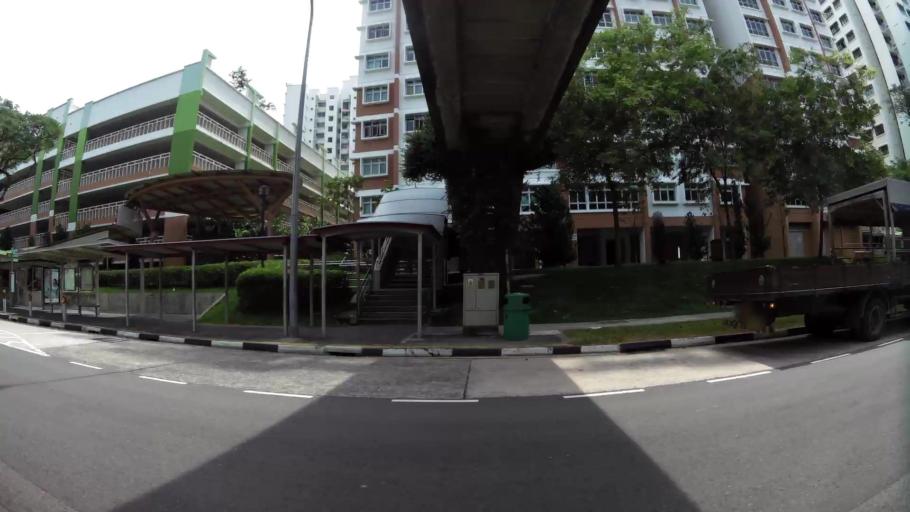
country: MY
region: Johor
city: Johor Bahru
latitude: 1.3495
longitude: 103.7088
